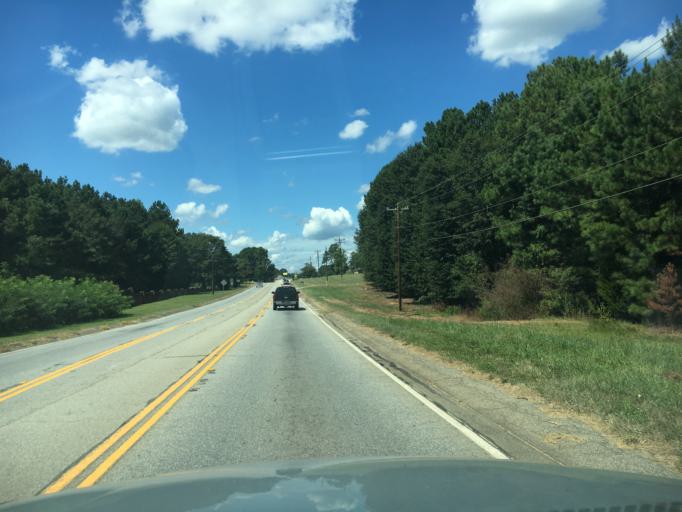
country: US
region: South Carolina
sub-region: Laurens County
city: Laurens
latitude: 34.5012
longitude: -82.0601
